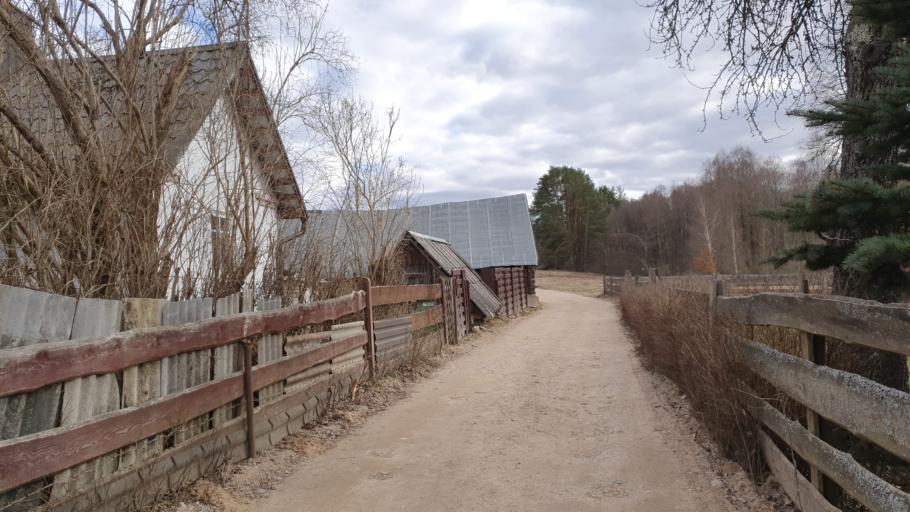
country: LT
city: Grigiskes
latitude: 54.7348
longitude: 25.0268
